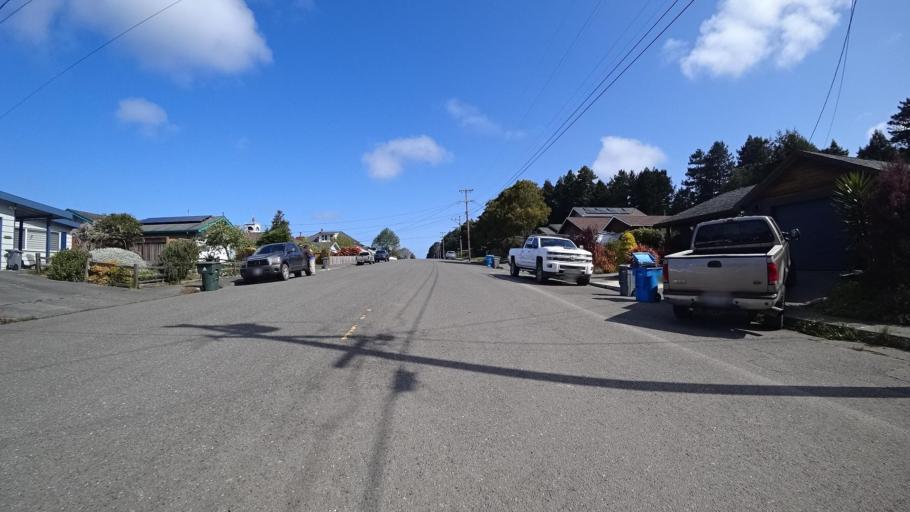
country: US
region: California
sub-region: Humboldt County
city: Cutten
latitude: 40.7751
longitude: -124.1602
